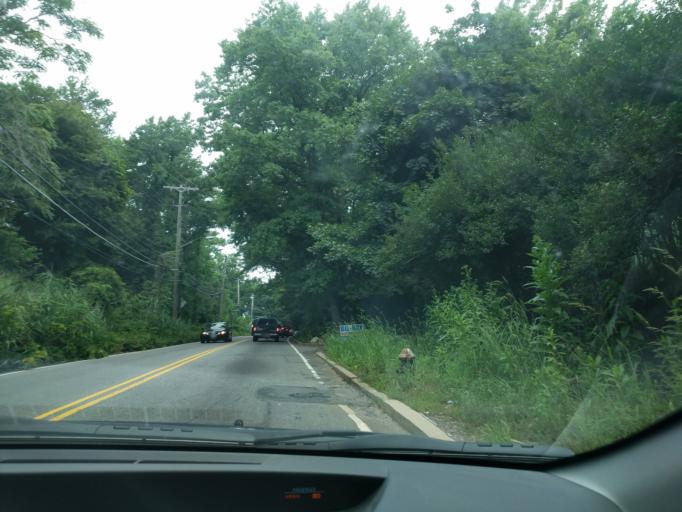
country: US
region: New York
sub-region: Richmond County
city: Staten Island
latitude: 40.6009
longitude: -74.1138
